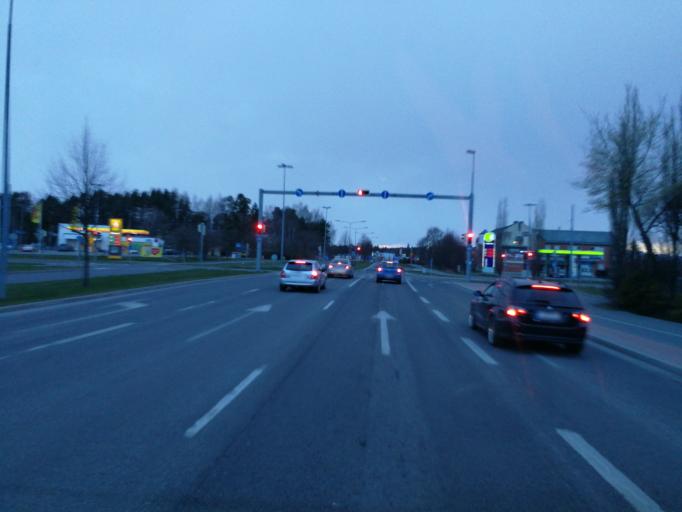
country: FI
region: Varsinais-Suomi
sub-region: Turku
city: Turku
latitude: 60.4696
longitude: 22.2367
